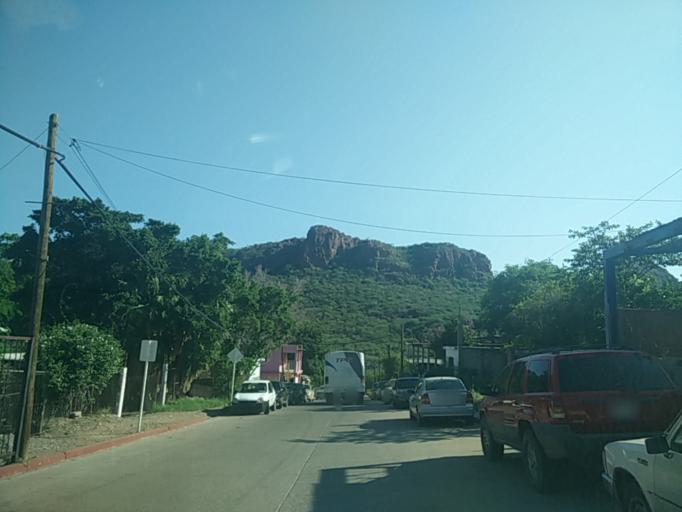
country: MX
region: Sonora
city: Heroica Guaymas
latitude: 27.9353
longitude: -110.8833
